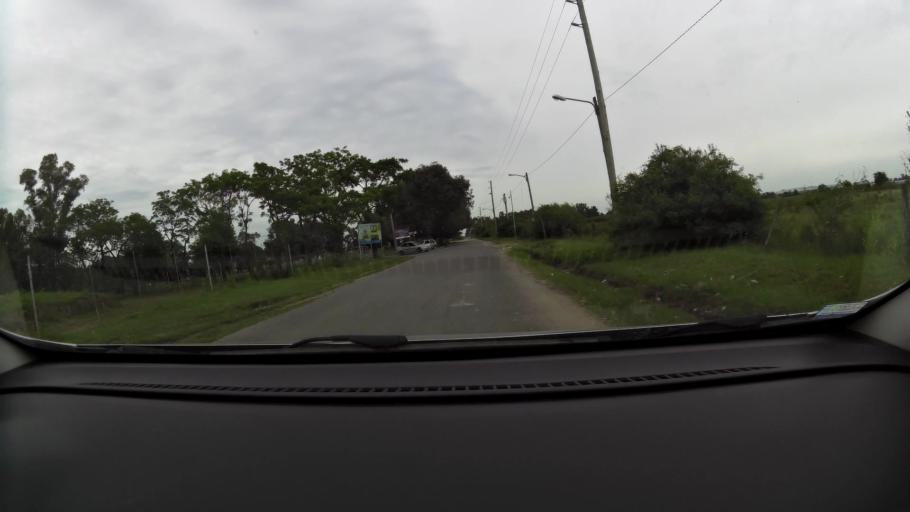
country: AR
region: Buenos Aires
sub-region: Partido de Campana
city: Campana
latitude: -34.2004
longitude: -58.9485
